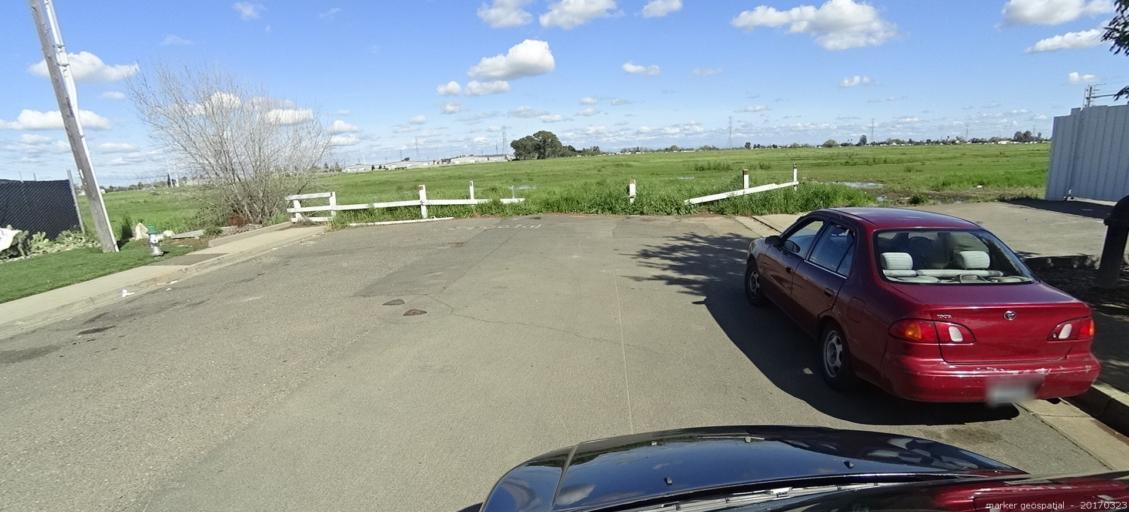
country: US
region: California
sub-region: Sacramento County
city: Florin
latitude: 38.5061
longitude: -121.3815
